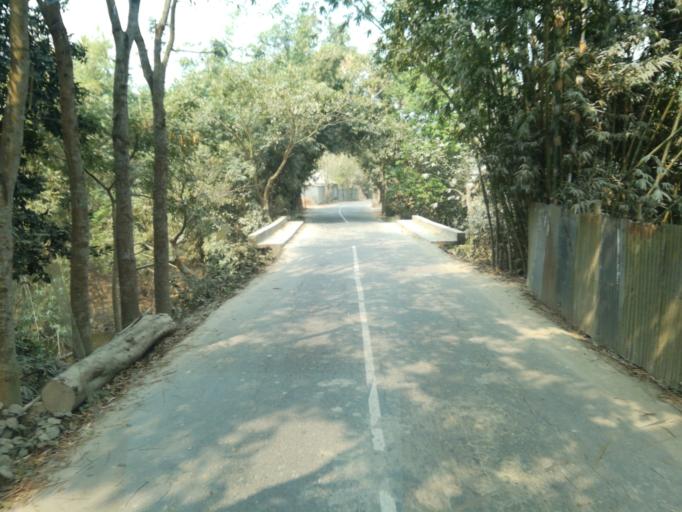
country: BD
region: Dhaka
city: Nagarpur
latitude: 23.9792
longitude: 89.8435
